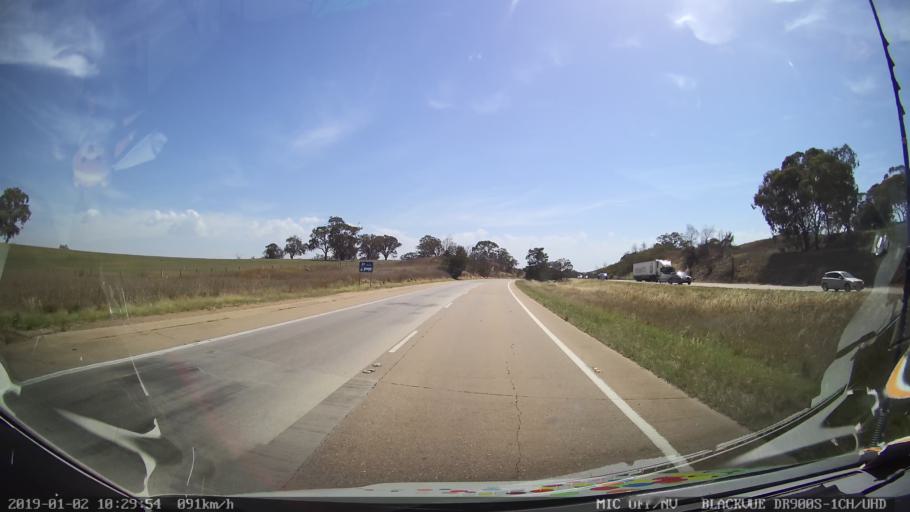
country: AU
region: New South Wales
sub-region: Gundagai
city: Gundagai
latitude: -34.8923
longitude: 148.2117
